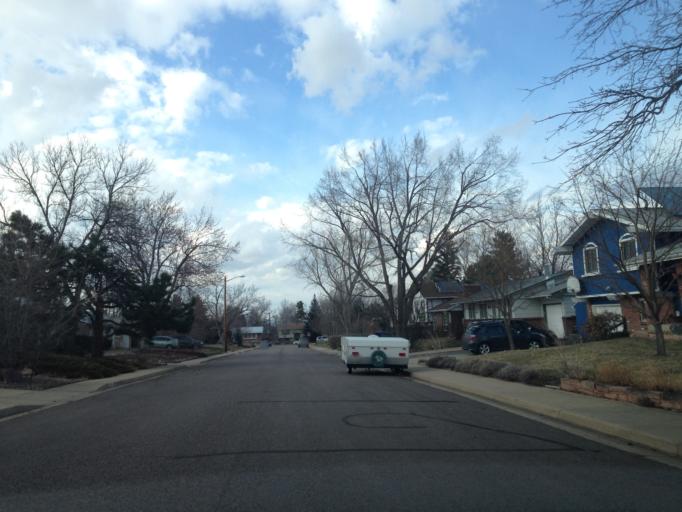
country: US
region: Colorado
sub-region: Boulder County
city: Boulder
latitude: 39.9771
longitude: -105.2521
